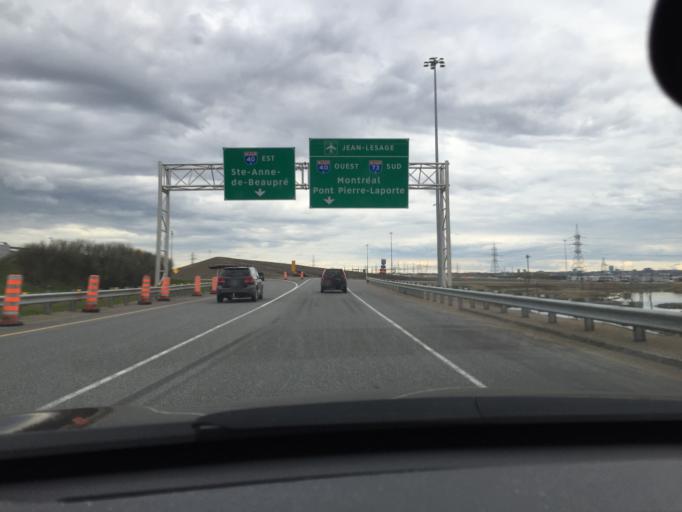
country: CA
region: Quebec
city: Quebec
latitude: 46.8394
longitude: -71.2670
